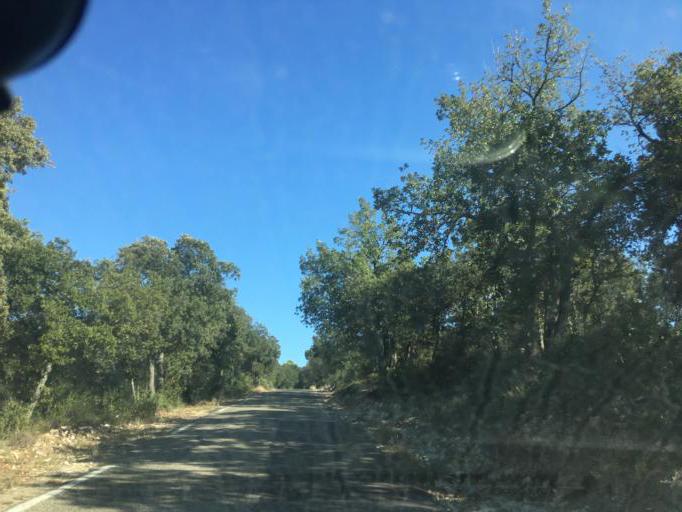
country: FR
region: Provence-Alpes-Cote d'Azur
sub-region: Departement du Var
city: Regusse
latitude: 43.7331
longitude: 6.1069
